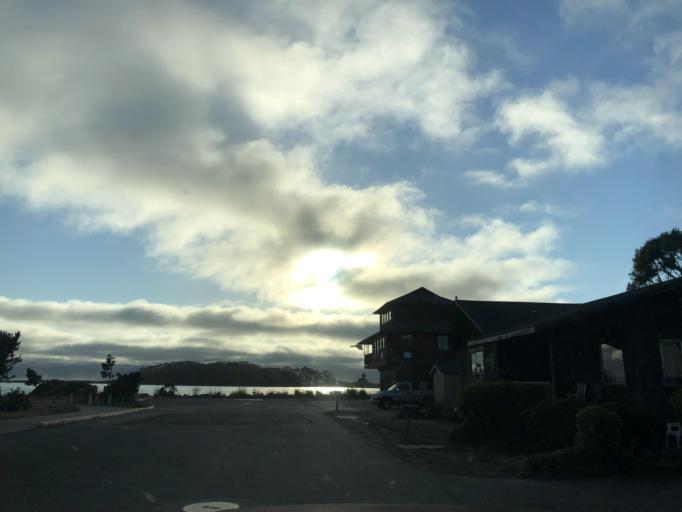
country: US
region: California
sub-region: Humboldt County
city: Bayview
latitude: 40.7765
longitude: -124.1932
